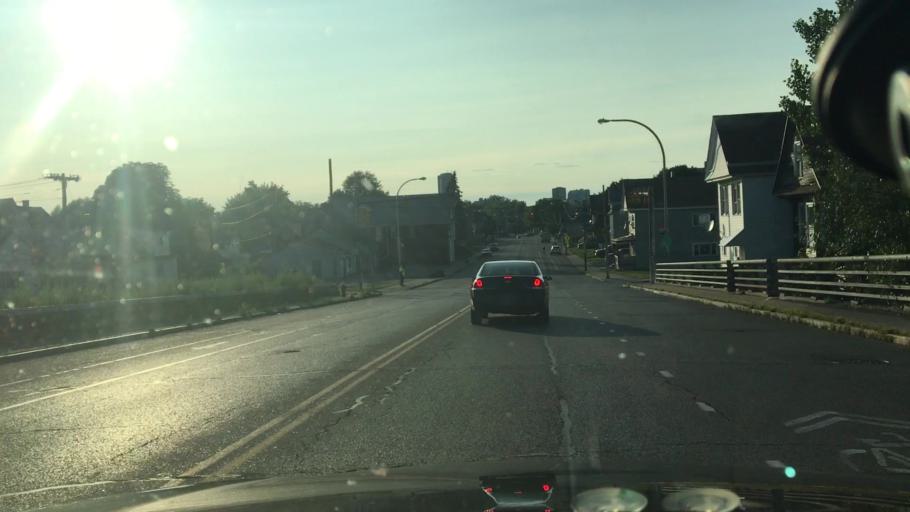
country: US
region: New York
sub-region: Erie County
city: Buffalo
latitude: 42.8657
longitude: -78.8471
